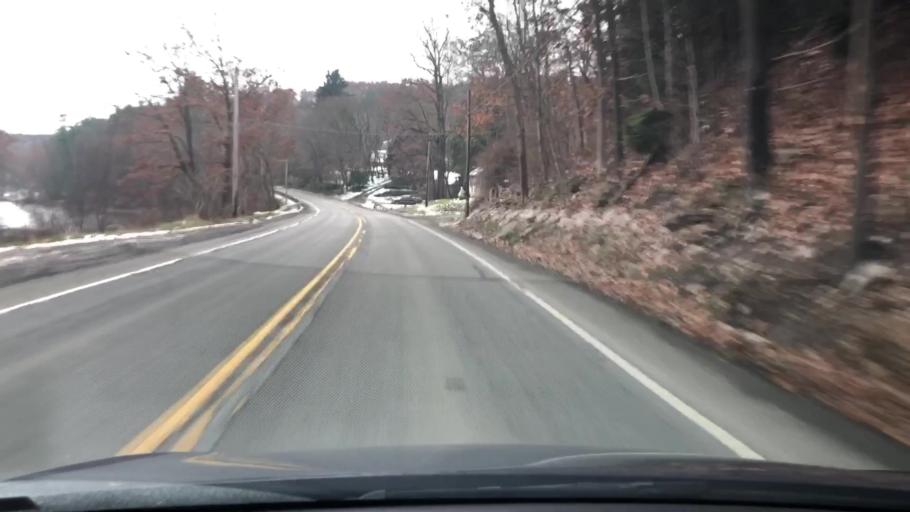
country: US
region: Pennsylvania
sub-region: Jefferson County
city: Brookville
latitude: 41.1340
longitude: -79.1555
